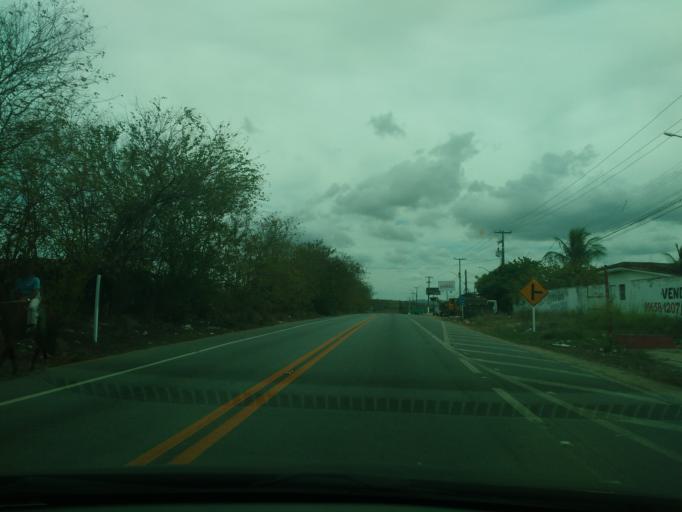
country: BR
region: Alagoas
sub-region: Uniao Dos Palmares
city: Uniao dos Palmares
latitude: -9.1676
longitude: -36.0220
